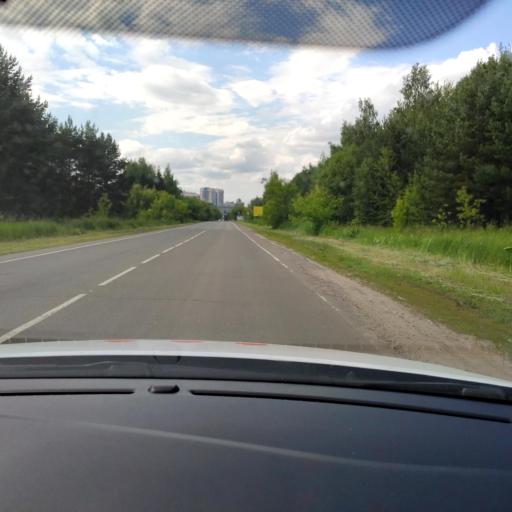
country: RU
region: Tatarstan
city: Stolbishchi
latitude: 55.7231
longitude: 49.2047
